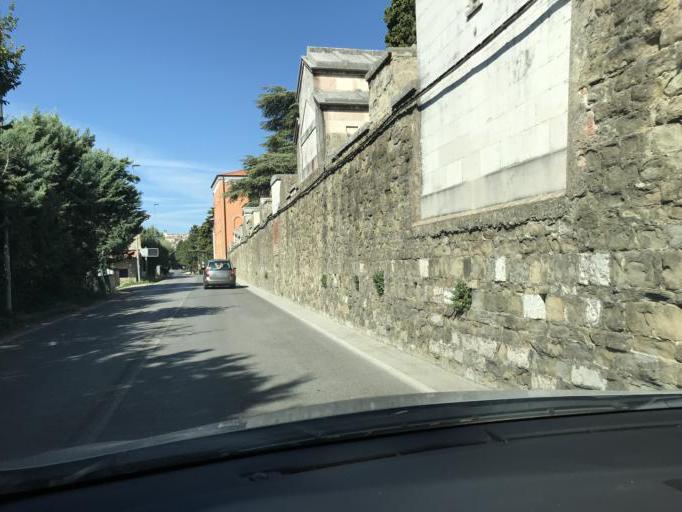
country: IT
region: Umbria
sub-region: Provincia di Perugia
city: Perugia
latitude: 43.1106
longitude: 12.4126
